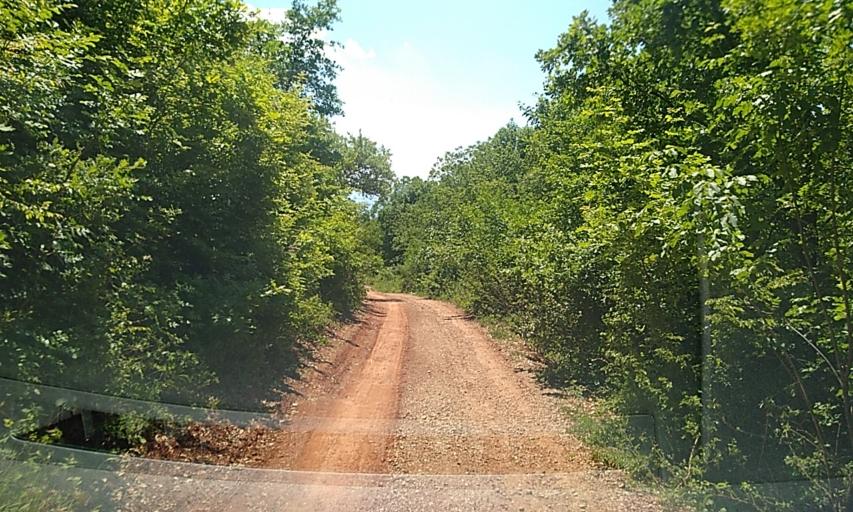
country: RS
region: Central Serbia
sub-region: Nisavski Okrug
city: Niska Banja
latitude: 43.3746
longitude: 21.9930
